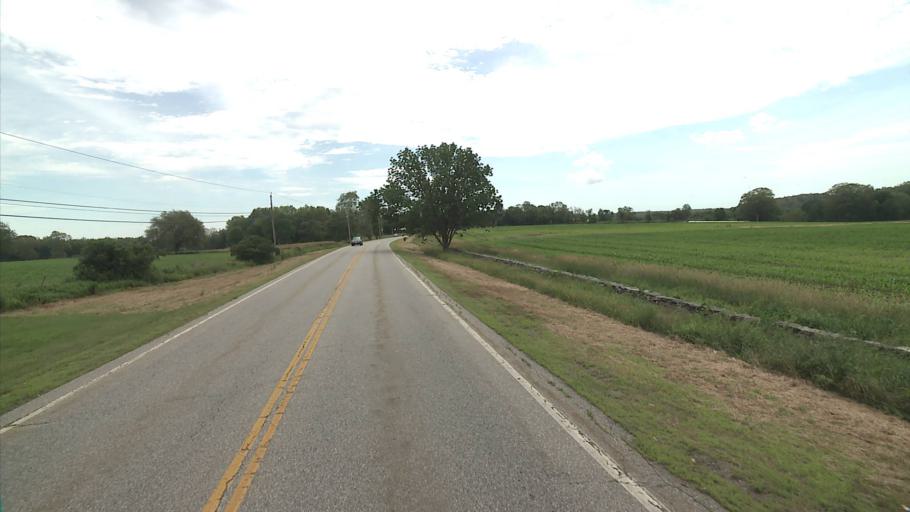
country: US
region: Connecticut
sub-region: New London County
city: Preston City
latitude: 41.5436
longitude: -71.9675
